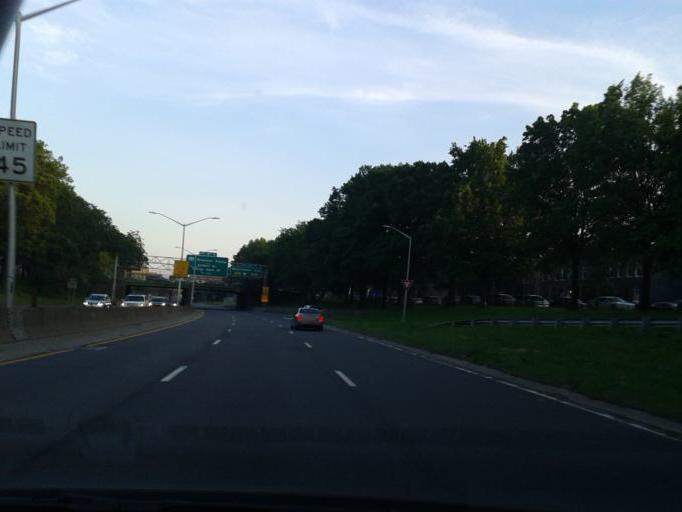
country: US
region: New York
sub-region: Bronx
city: The Bronx
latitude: 40.8339
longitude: -73.8743
